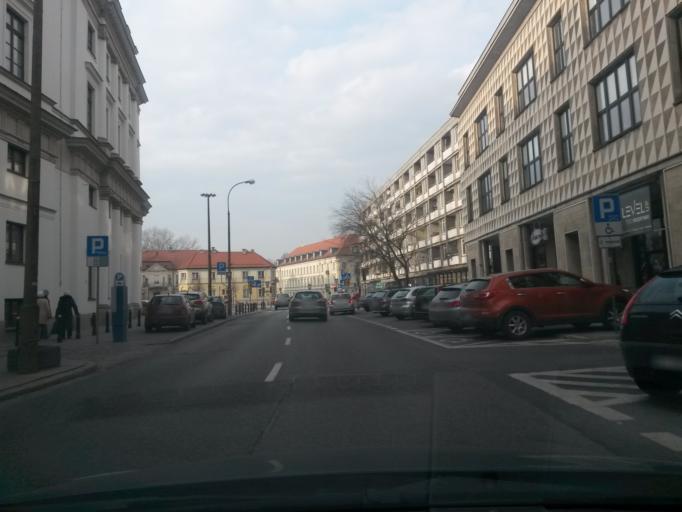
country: PL
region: Masovian Voivodeship
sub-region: Warszawa
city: Warsaw
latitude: 52.2440
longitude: 21.0116
